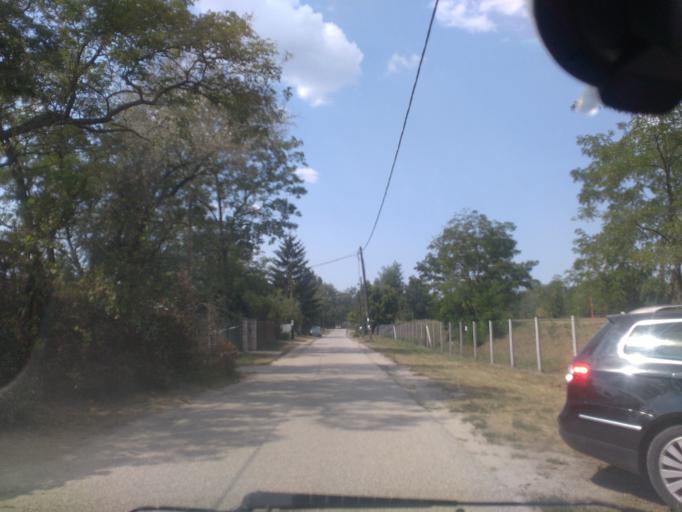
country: HU
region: Komarom-Esztergom
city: Pilismarot
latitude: 47.7993
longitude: 18.8944
